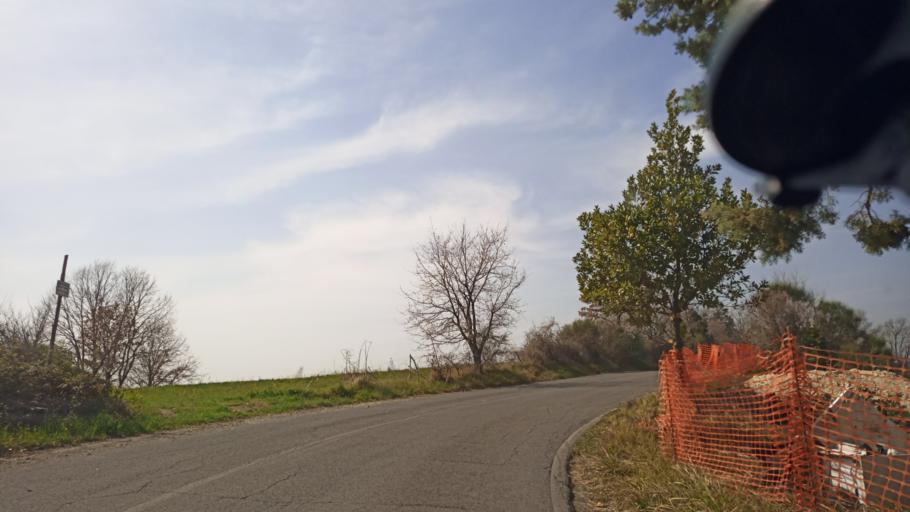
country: IT
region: Latium
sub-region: Provincia di Rieti
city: Montasola
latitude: 42.3639
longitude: 12.6722
